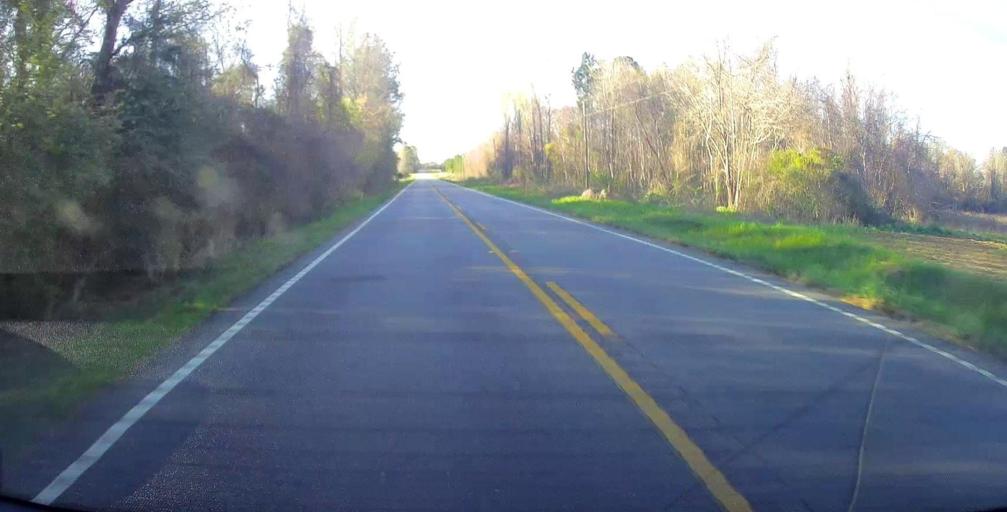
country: US
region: Georgia
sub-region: Pulaski County
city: Hawkinsville
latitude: 32.2236
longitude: -83.3902
